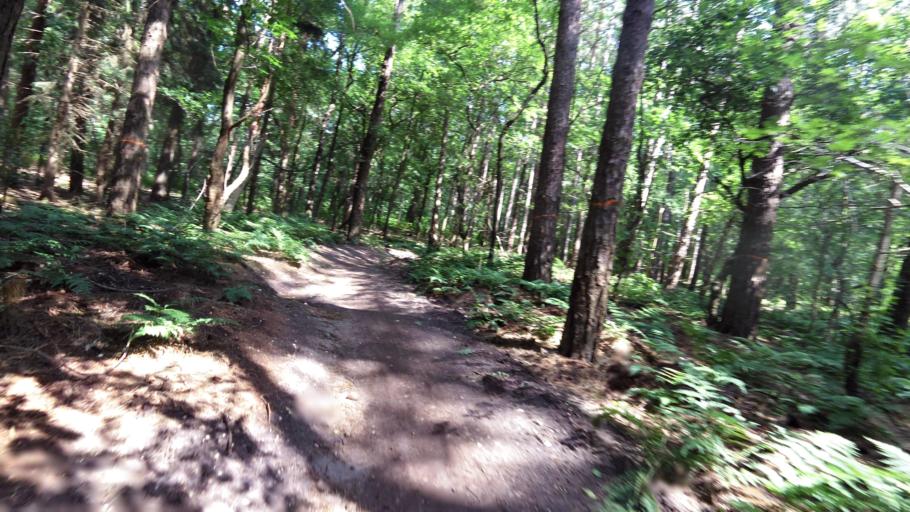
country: NL
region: Gelderland
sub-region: Gemeente Renkum
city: Oosterbeek
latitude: 51.9993
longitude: 5.8308
